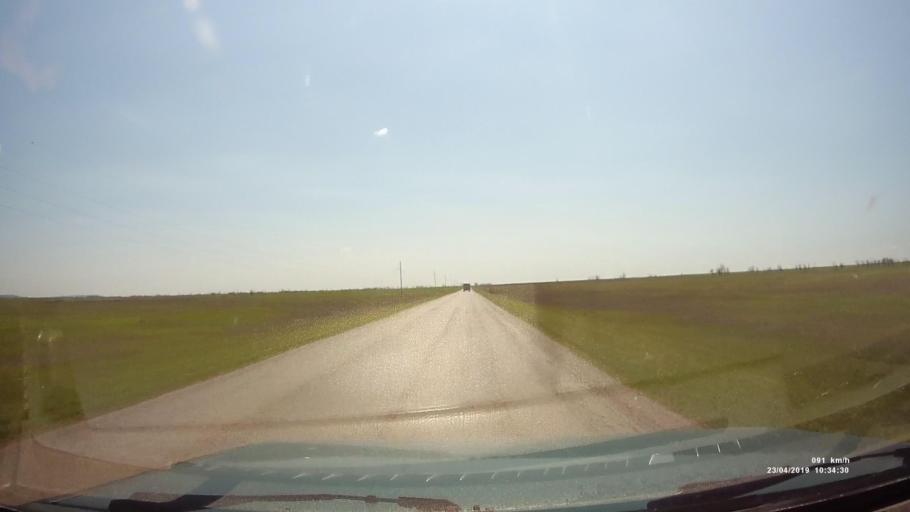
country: RU
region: Kalmykiya
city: Yashalta
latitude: 46.5634
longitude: 42.6111
